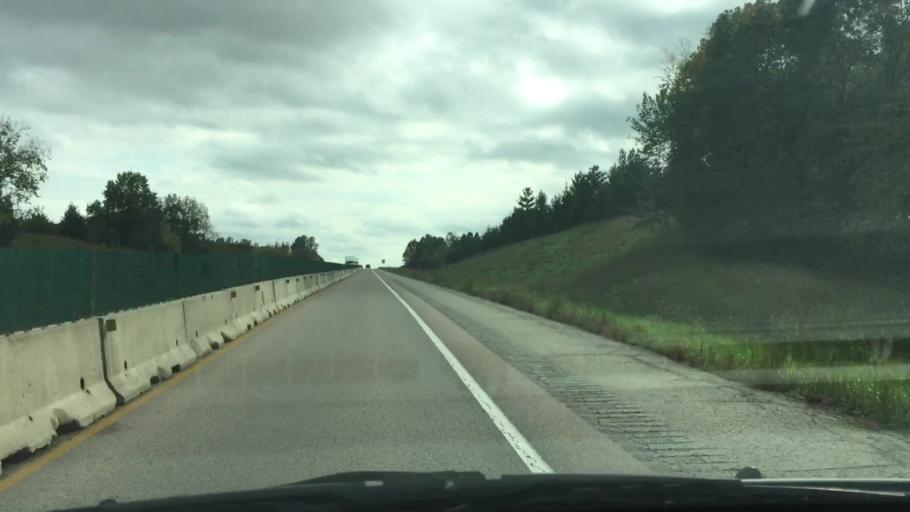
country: US
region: Iowa
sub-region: Decatur County
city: Leon
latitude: 40.6940
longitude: -93.8462
